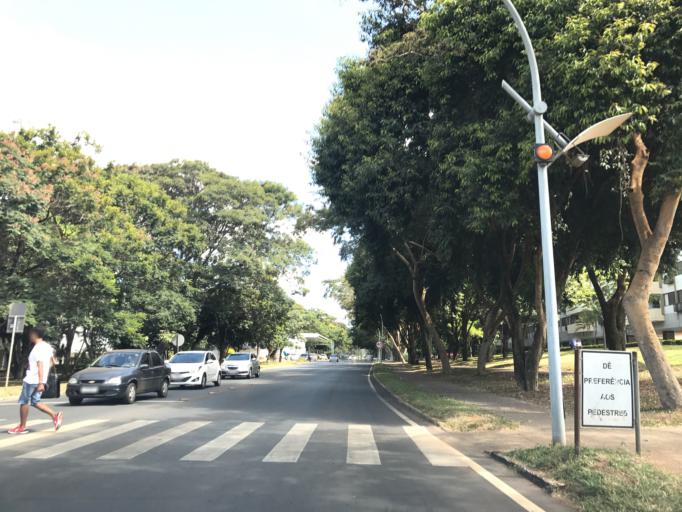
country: BR
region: Federal District
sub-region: Brasilia
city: Brasilia
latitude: -15.8338
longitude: -47.9182
